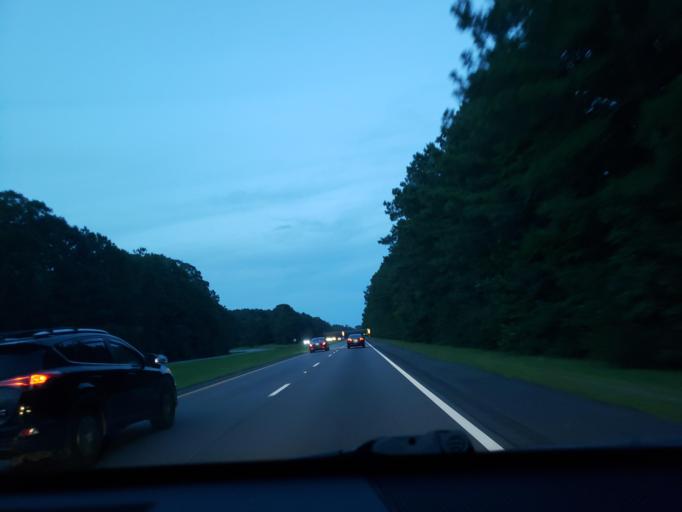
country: US
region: Virginia
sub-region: City of Franklin
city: Franklin
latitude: 36.6450
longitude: -76.8786
